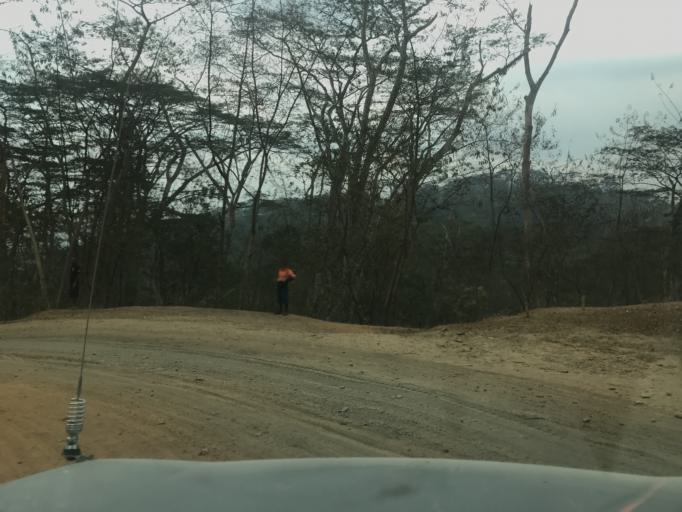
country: TL
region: Ermera
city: Gleno
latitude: -8.7606
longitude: 125.4310
